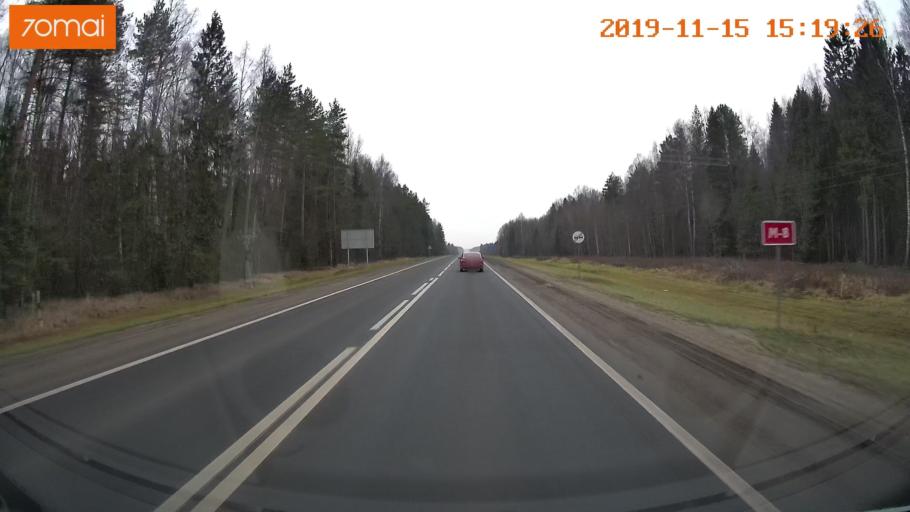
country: RU
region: Jaroslavl
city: Danilov
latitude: 58.2344
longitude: 40.1778
